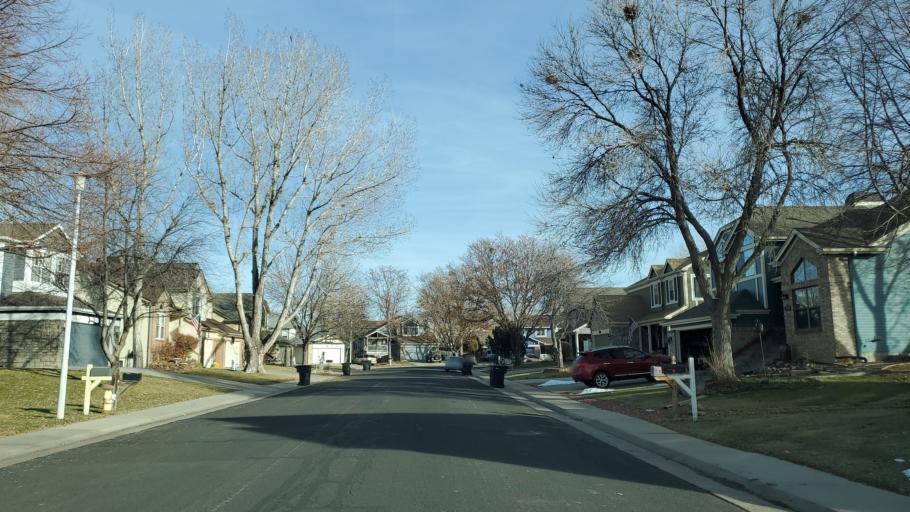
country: US
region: Colorado
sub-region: Adams County
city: Northglenn
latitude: 39.9053
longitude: -104.9522
